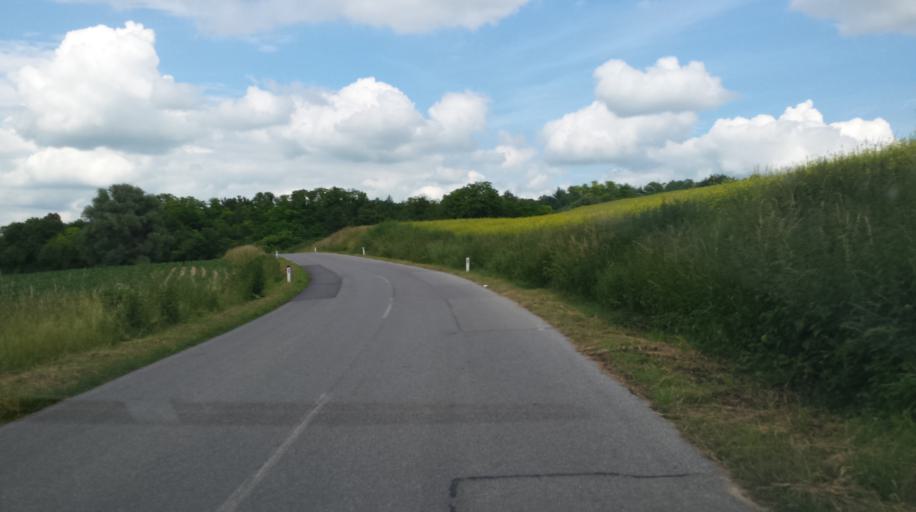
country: AT
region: Lower Austria
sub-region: Politischer Bezirk Mistelbach
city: Hochleithen
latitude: 48.4360
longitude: 16.5008
